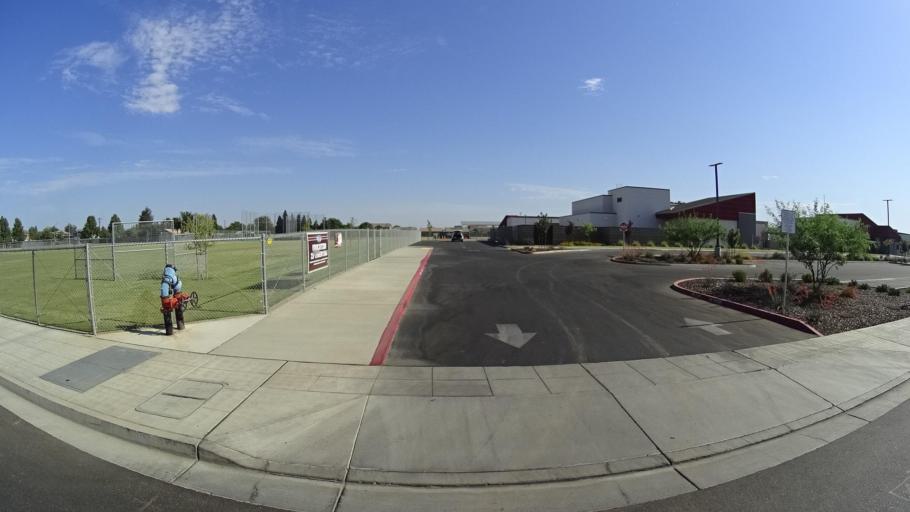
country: US
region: California
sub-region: Fresno County
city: Tarpey Village
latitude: 36.7813
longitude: -119.6531
